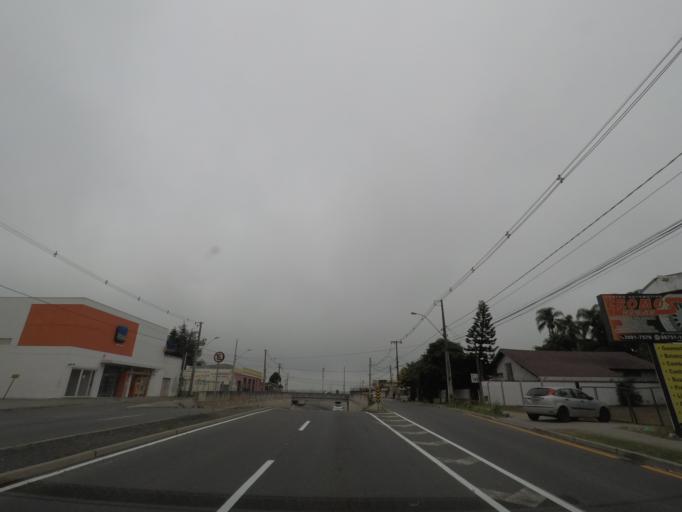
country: BR
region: Parana
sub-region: Sao Jose Dos Pinhais
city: Sao Jose dos Pinhais
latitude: -25.5302
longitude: -49.2017
